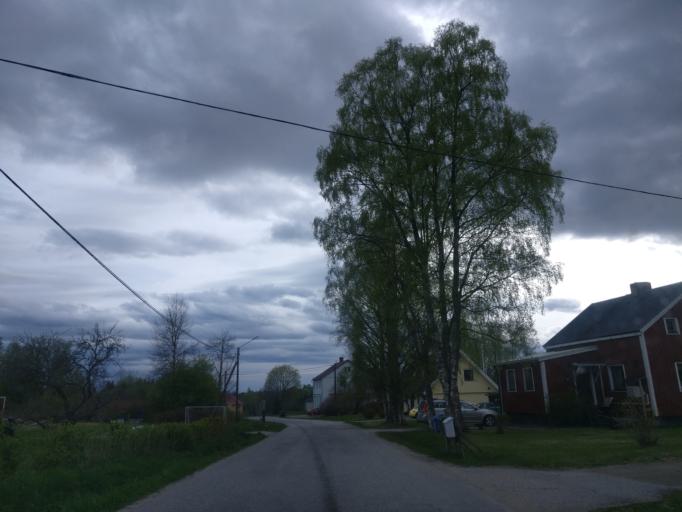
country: SE
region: Vaesternorrland
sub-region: Timra Kommun
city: Soraker
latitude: 62.5132
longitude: 17.5152
